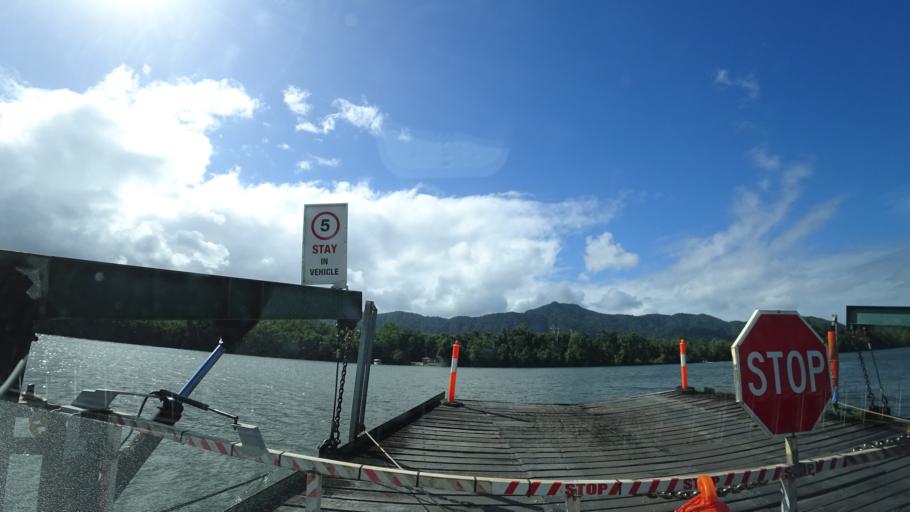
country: AU
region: Queensland
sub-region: Cairns
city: Port Douglas
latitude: -16.2603
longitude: 145.3979
